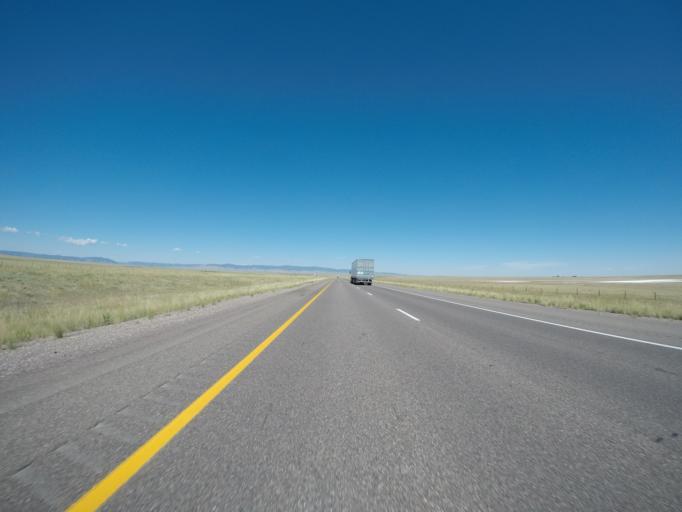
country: US
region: Wyoming
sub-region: Albany County
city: Laramie
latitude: 41.3613
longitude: -105.7680
